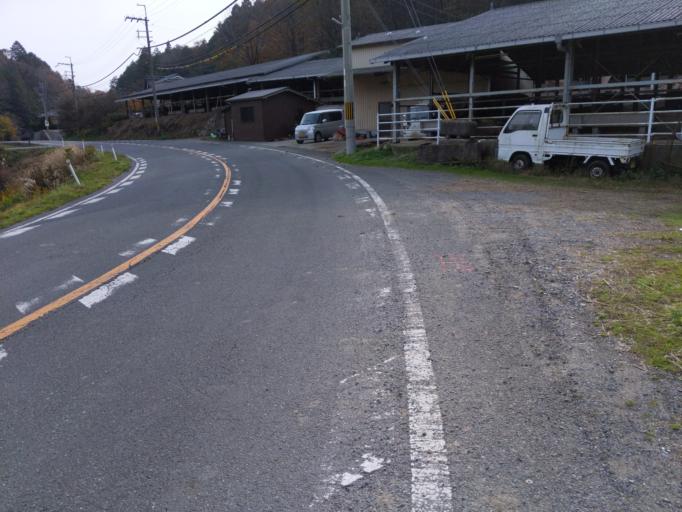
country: JP
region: Kyoto
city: Kameoka
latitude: 34.9730
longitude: 135.5121
